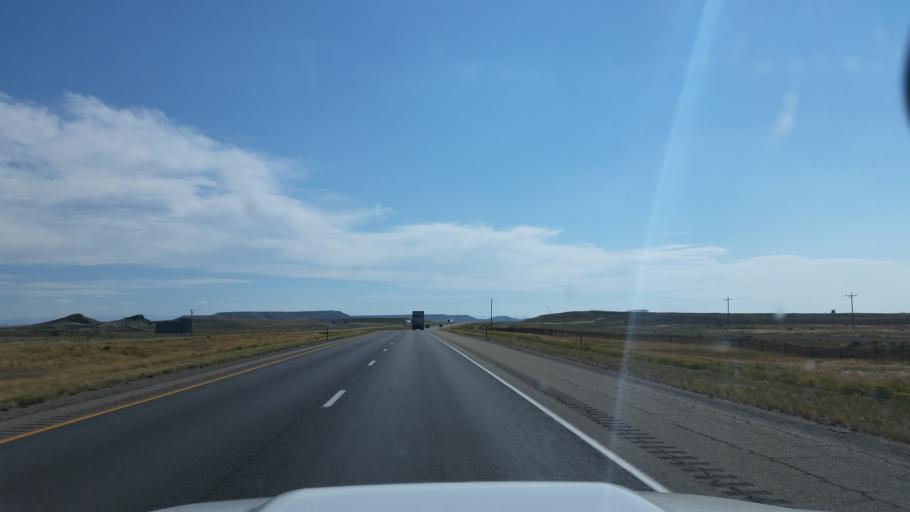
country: US
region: Wyoming
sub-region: Uinta County
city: Lyman
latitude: 41.4740
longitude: -110.0357
